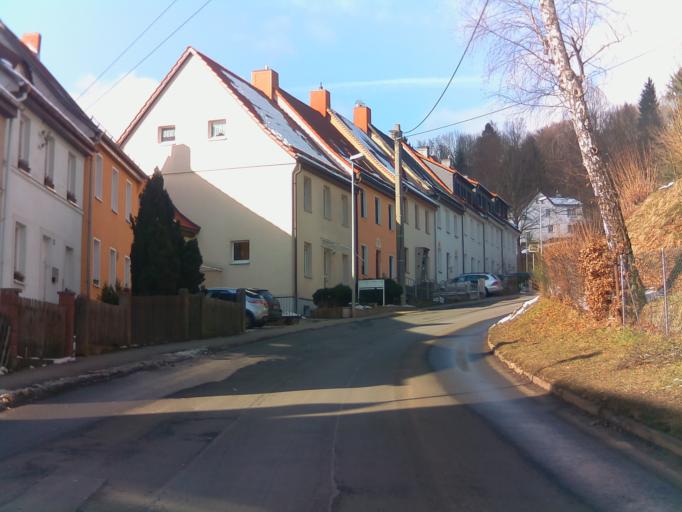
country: DE
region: Thuringia
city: Suhl
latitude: 50.6105
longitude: 10.6780
